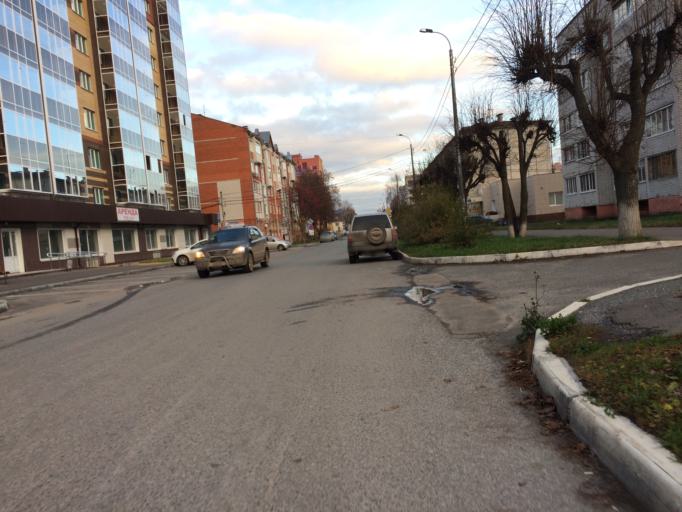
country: RU
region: Mariy-El
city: Yoshkar-Ola
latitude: 56.6479
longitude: 47.8937
